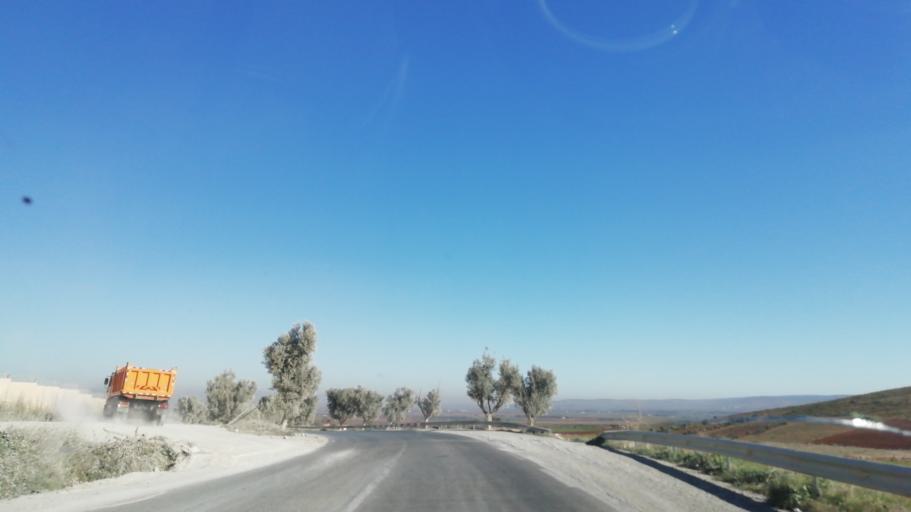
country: DZ
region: Mascara
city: Mascara
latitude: 35.2521
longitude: 0.1226
